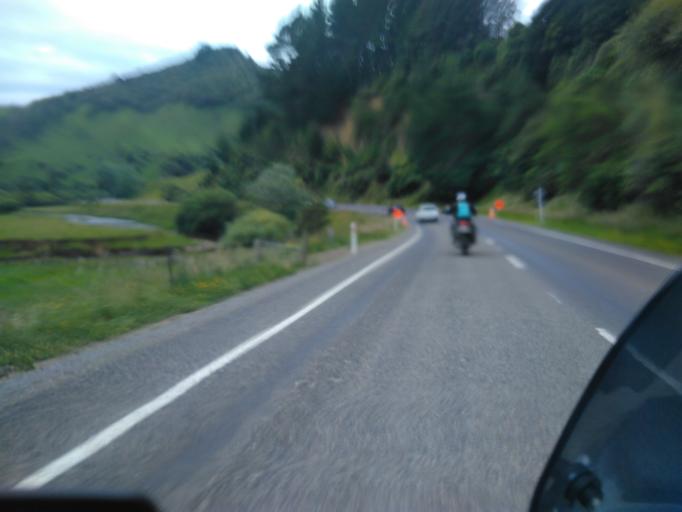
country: NZ
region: Bay of Plenty
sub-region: Opotiki District
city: Opotiki
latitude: -38.3773
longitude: 177.4809
